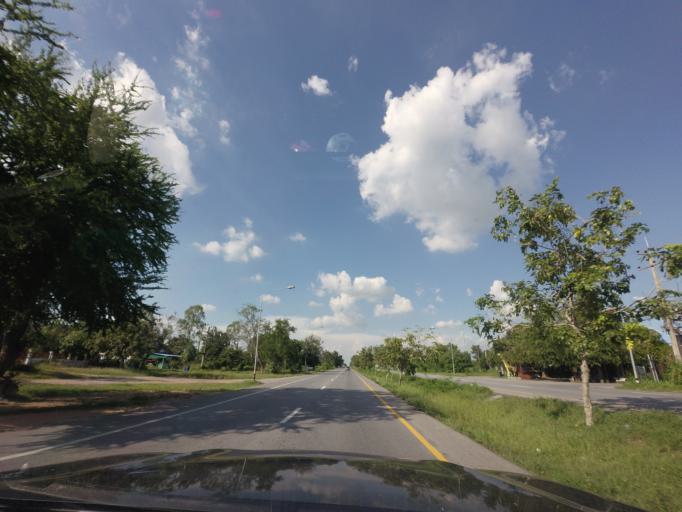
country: TH
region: Khon Kaen
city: Phon
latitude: 15.7270
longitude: 102.5939
